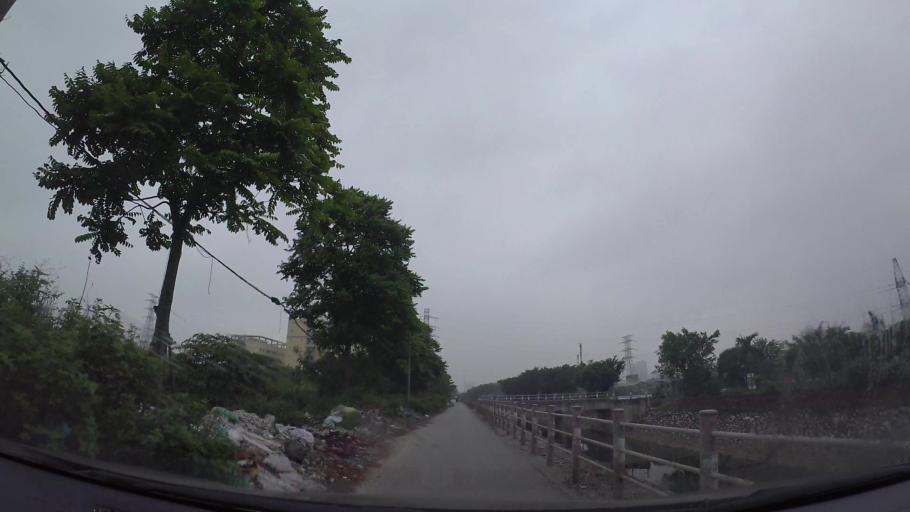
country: VN
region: Ha Noi
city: Hai BaTrung
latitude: 20.9795
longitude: 105.8676
